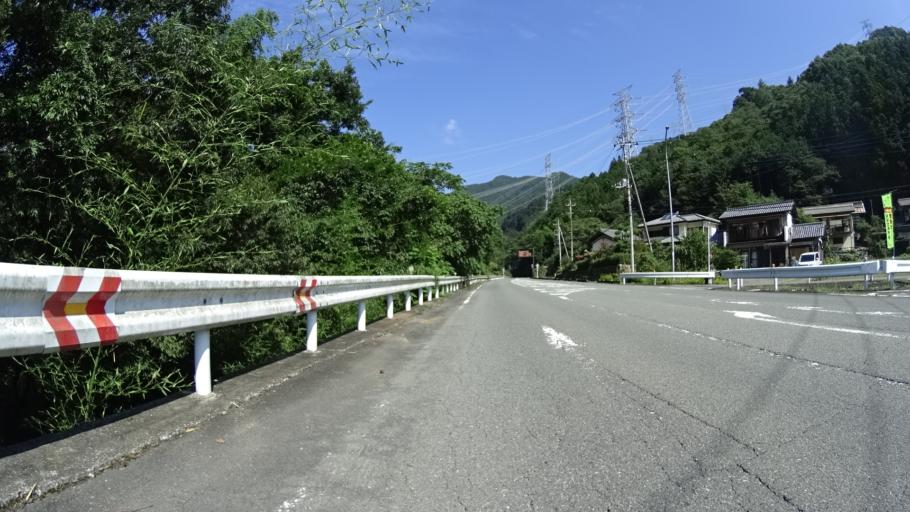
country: JP
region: Saitama
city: Chichibu
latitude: 36.0294
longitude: 138.9402
